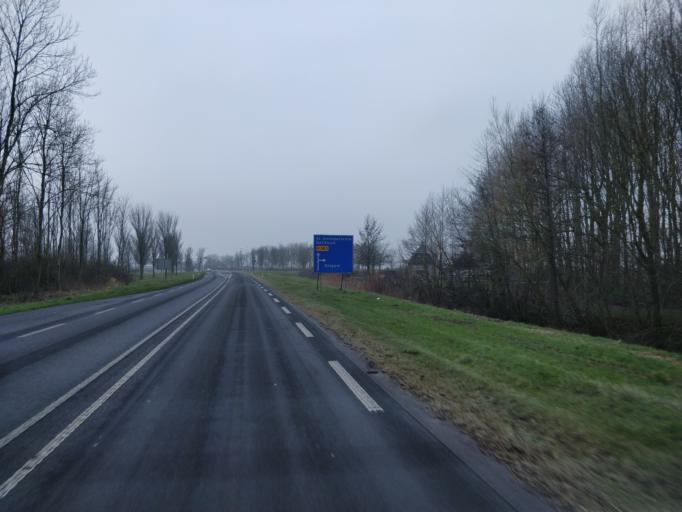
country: NL
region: Friesland
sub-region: Menameradiel
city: Menaam
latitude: 53.2370
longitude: 5.6811
